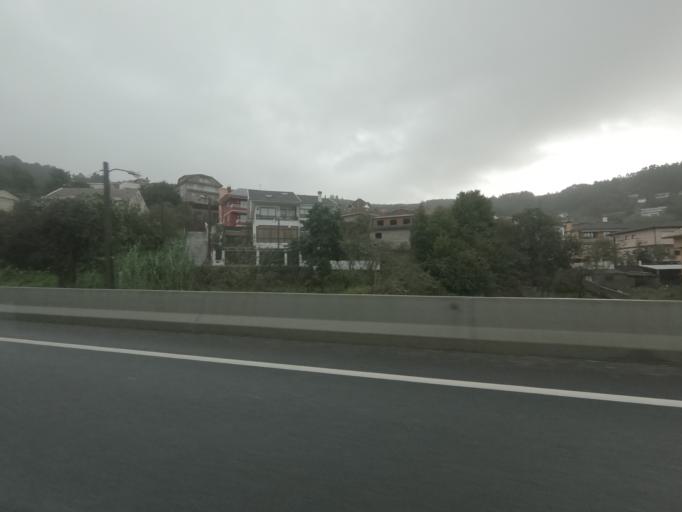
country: ES
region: Galicia
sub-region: Provincia de Pontevedra
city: Vigo
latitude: 42.2677
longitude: -8.6880
